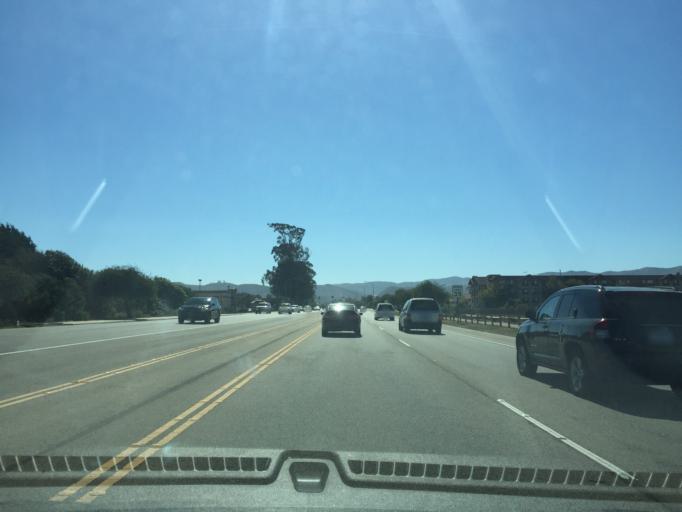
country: US
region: California
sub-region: Santa Barbara County
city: Lompoc
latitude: 34.6659
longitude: -120.4578
